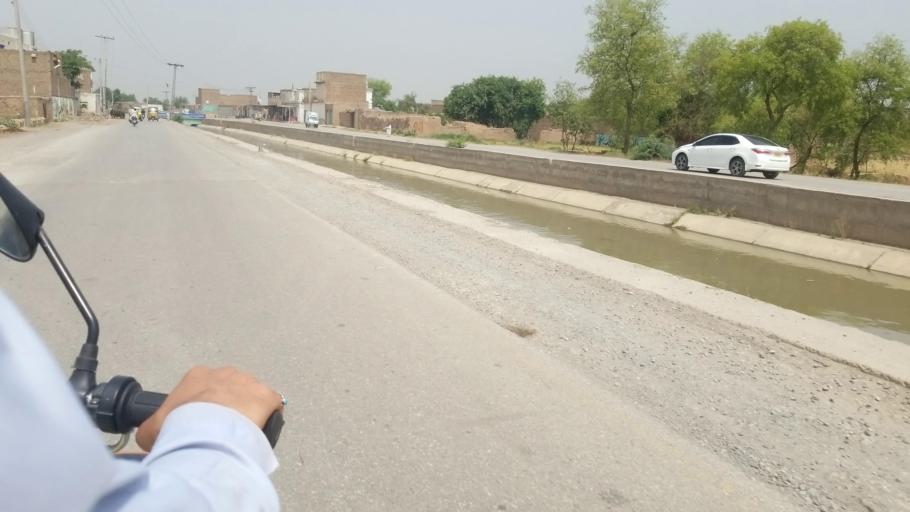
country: PK
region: Khyber Pakhtunkhwa
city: Peshawar
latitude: 33.9549
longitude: 71.5508
